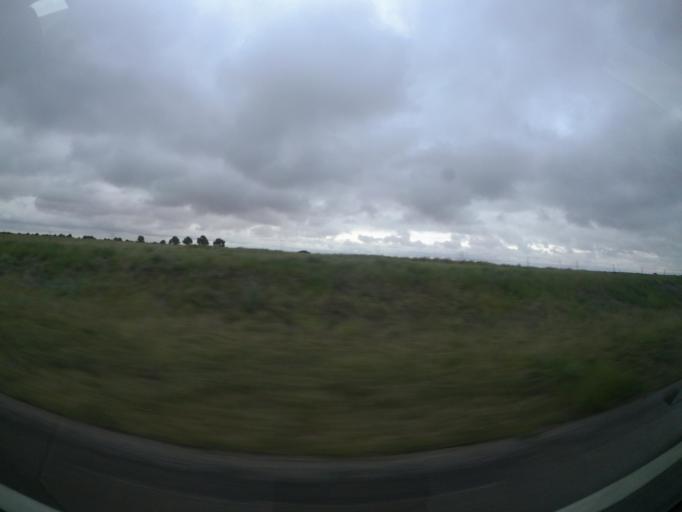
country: US
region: Colorado
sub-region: Yuma County
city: Yuma
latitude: 39.6702
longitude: -102.8914
